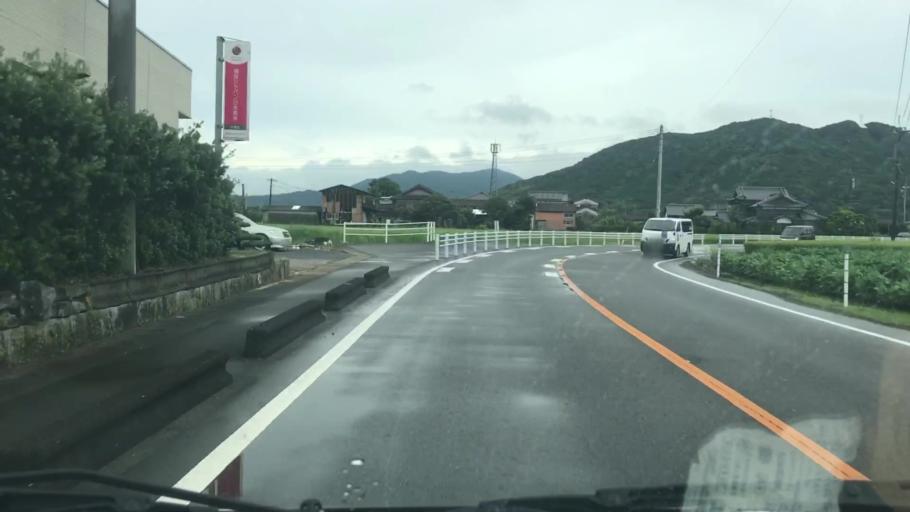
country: JP
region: Saga Prefecture
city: Takeocho-takeo
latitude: 33.1964
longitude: 130.0427
